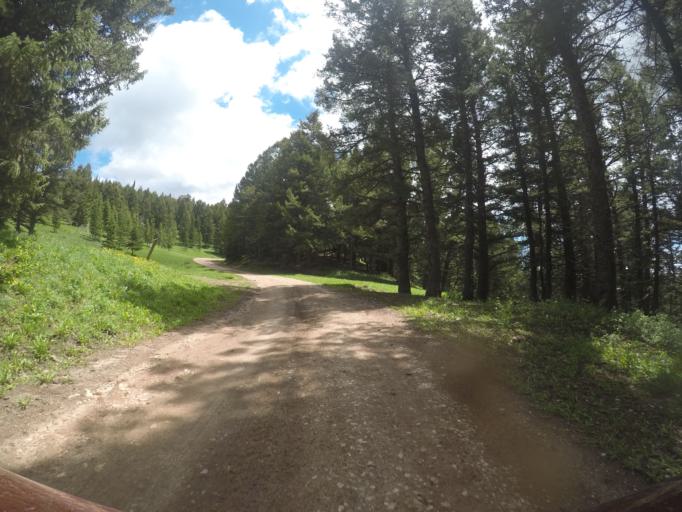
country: US
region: Wyoming
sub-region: Big Horn County
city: Lovell
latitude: 45.1693
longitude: -108.4226
